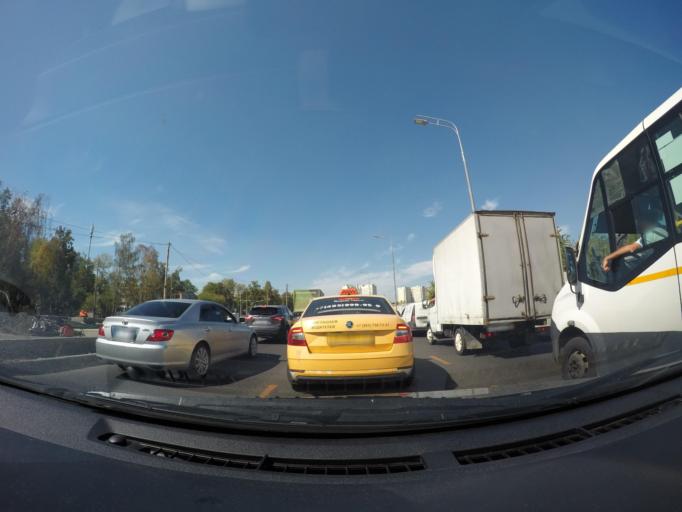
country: RU
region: Moskovskaya
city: Lyubertsy
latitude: 55.6837
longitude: 37.8839
